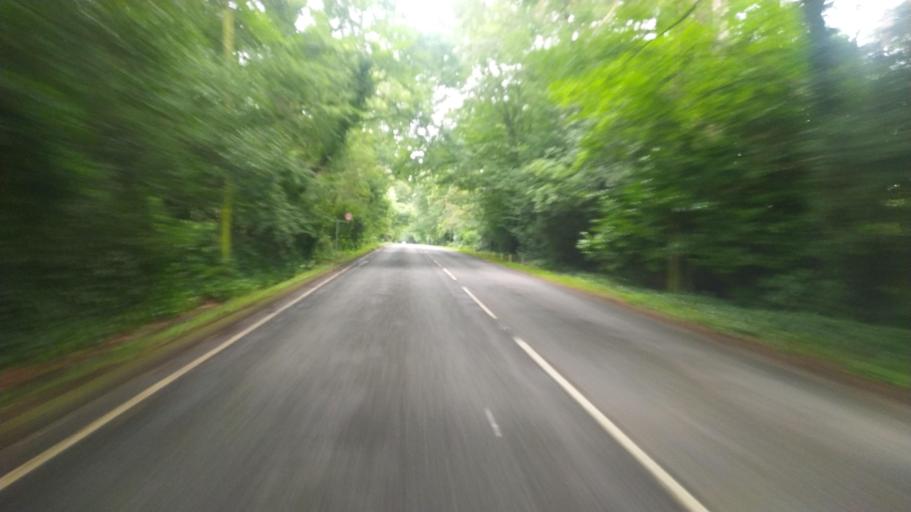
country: GB
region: England
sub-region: Hampshire
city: Liss
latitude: 51.0347
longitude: -0.8709
